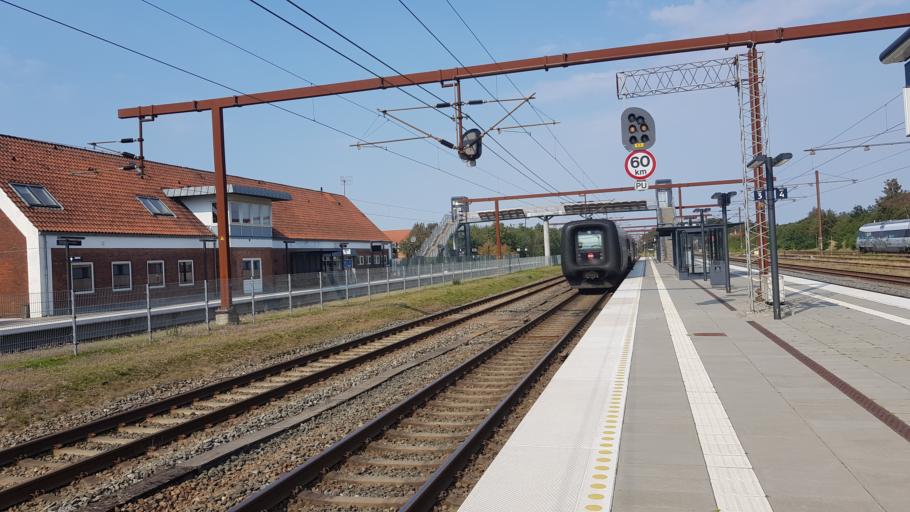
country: DK
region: South Denmark
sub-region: Aabenraa Kommune
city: Tinglev
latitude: 54.9359
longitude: 9.2583
